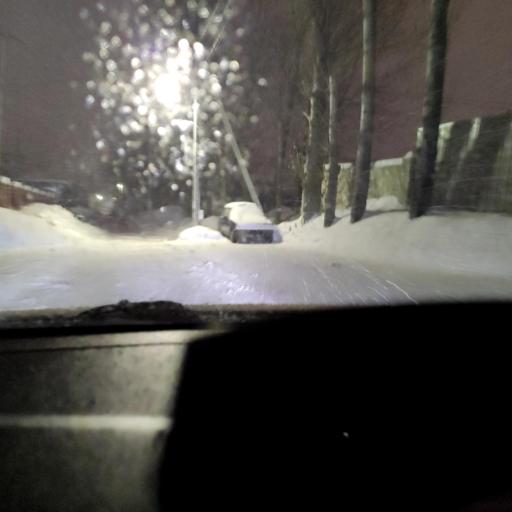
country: RU
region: Tatarstan
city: Stolbishchi
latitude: 55.7509
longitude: 49.2864
